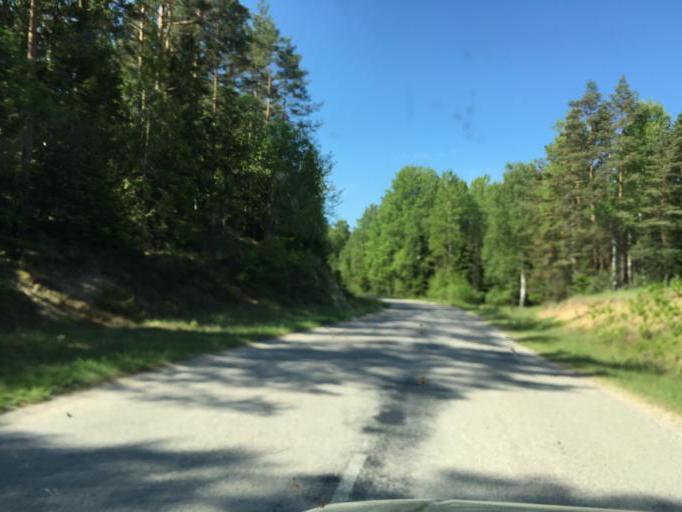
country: LV
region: Ventspils
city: Ventspils
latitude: 57.5084
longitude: 21.8510
